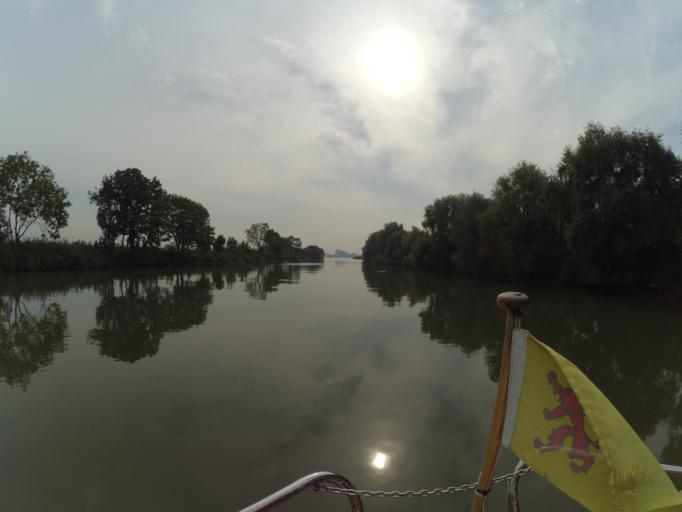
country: NL
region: South Holland
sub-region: Gemeente Papendrecht
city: Papendrecht
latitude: 51.8335
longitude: 4.6634
